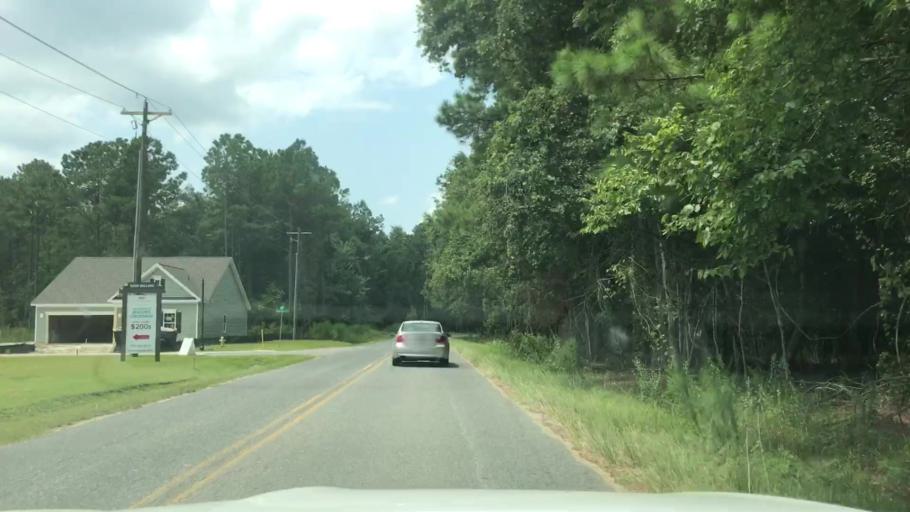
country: US
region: South Carolina
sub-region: Charleston County
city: Shell Point
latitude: 32.8153
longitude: -80.0872
